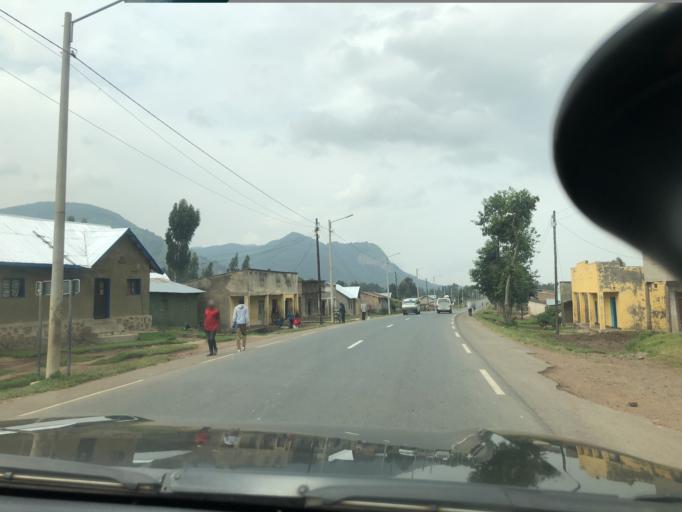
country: RW
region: Western Province
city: Gisenyi
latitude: -1.6337
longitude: 29.4118
